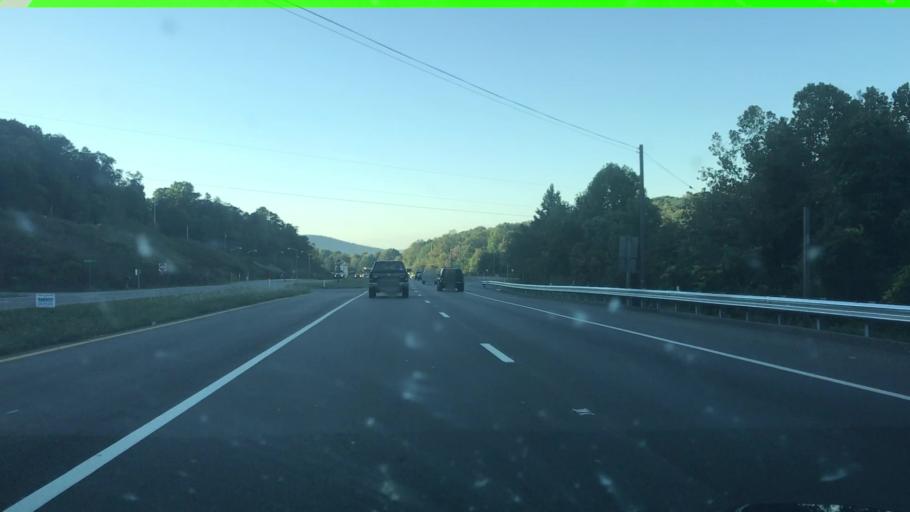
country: US
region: Virginia
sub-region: Botetourt County
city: Cloverdale
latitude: 37.3503
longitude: -79.8834
